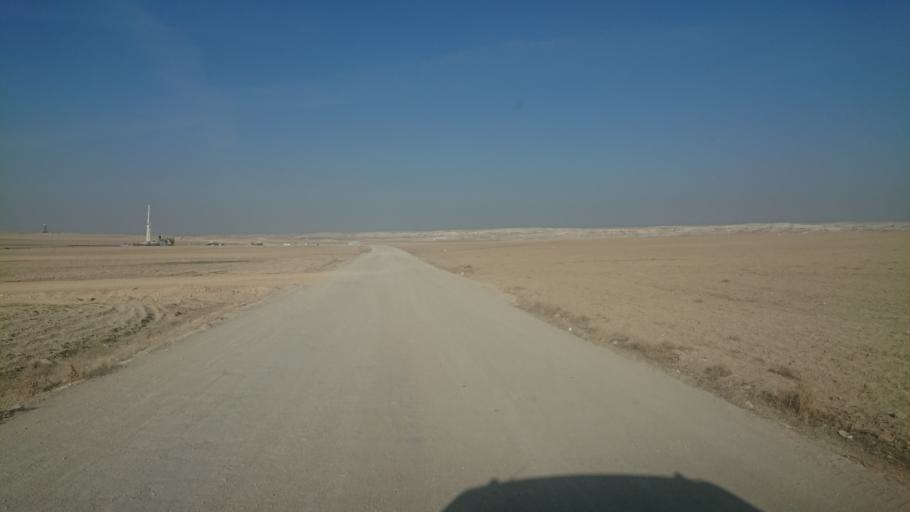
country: TR
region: Aksaray
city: Sultanhani
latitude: 38.0592
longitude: 33.6141
